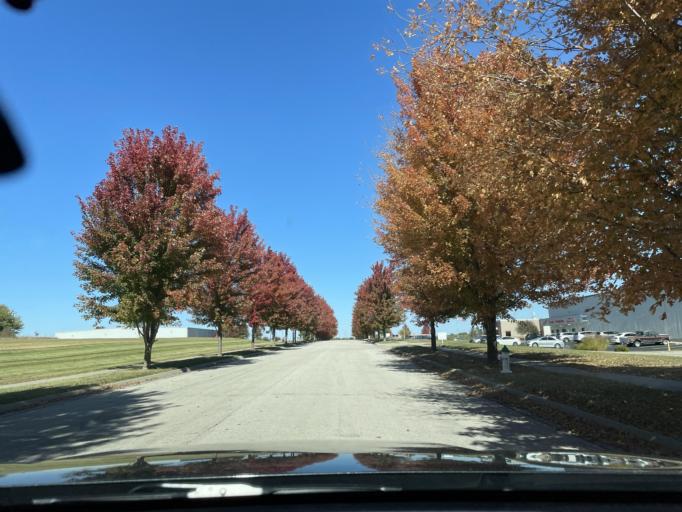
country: US
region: Missouri
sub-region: Buchanan County
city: Saint Joseph
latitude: 39.7524
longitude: -94.7568
